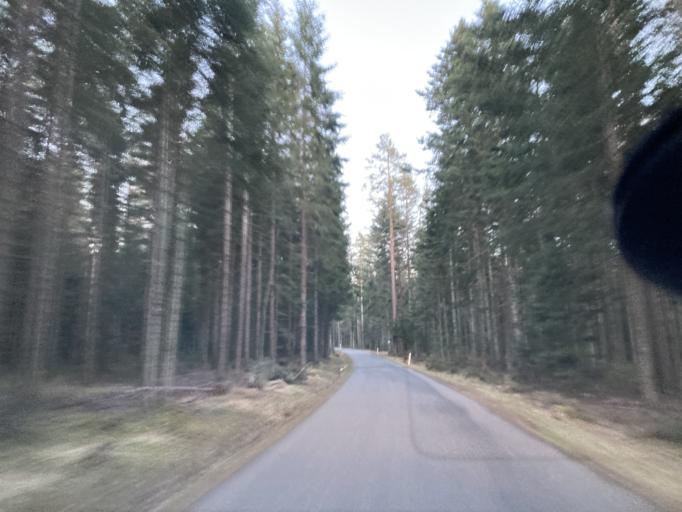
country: DE
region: Baden-Wuerttemberg
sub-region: Karlsruhe Region
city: Neuweiler
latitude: 48.6879
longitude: 8.5978
